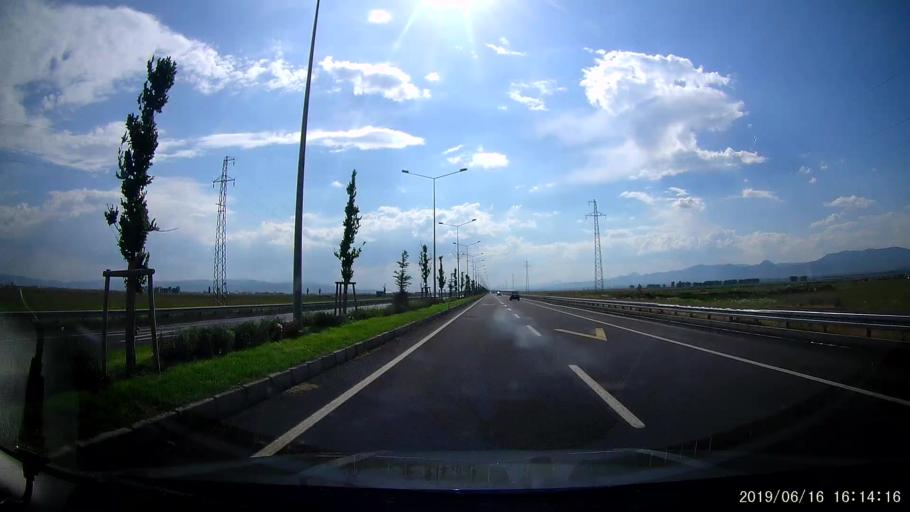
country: TR
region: Erzurum
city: Erzurum
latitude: 39.9605
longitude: 41.2536
